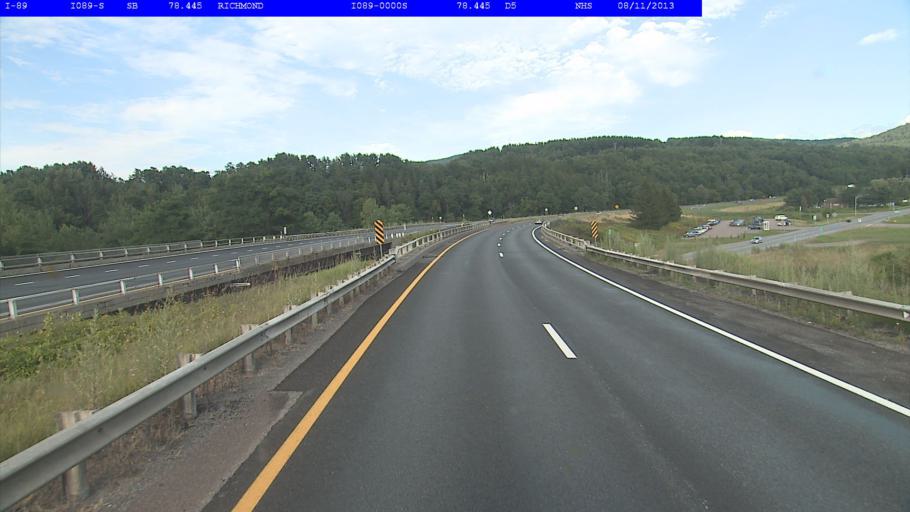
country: US
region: Vermont
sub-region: Chittenden County
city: Williston
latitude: 44.4238
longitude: -73.0109
